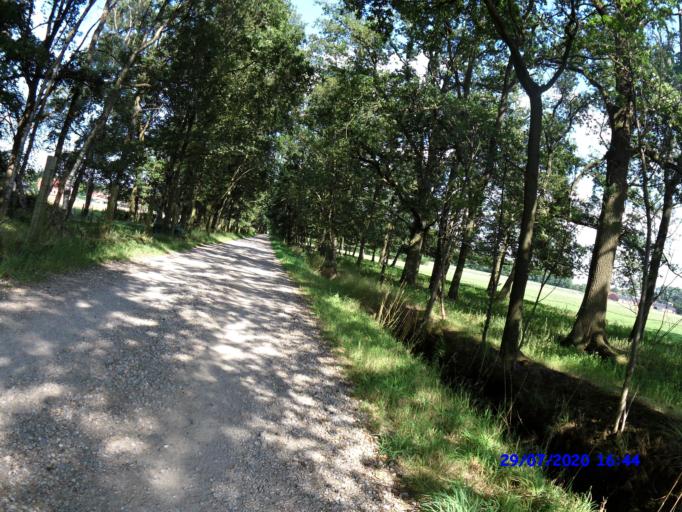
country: BE
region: Flanders
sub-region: Provincie Antwerpen
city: Rijkevorsel
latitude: 51.3098
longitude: 4.7869
